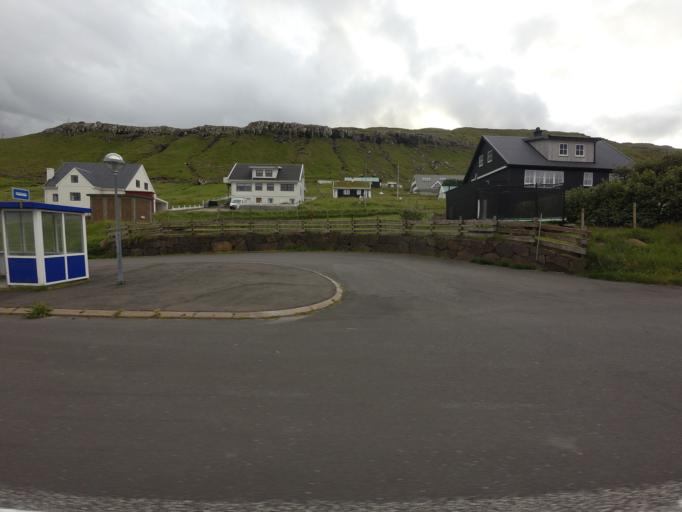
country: FO
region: Streymoy
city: Kollafjordhur
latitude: 62.1245
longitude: -6.8748
